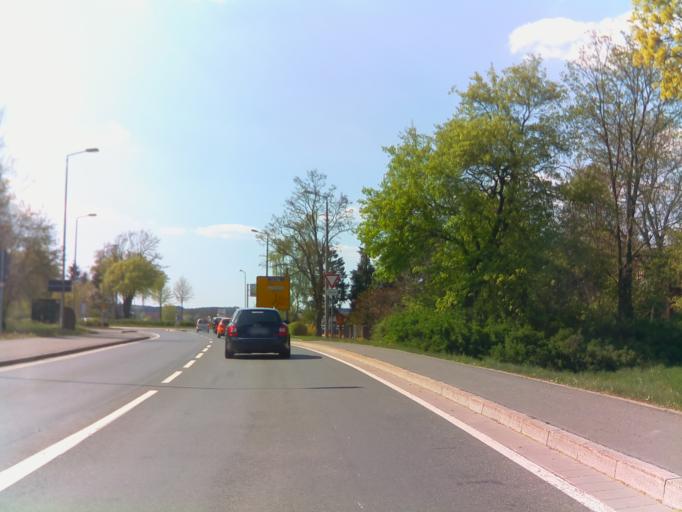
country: DE
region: Saxony
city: Syrau
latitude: 50.5352
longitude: 12.1028
